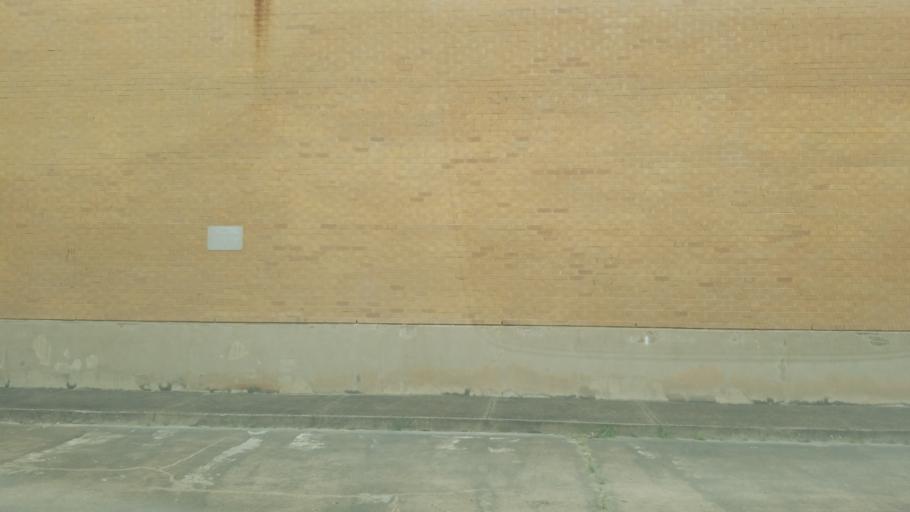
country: US
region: Texas
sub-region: Dallas County
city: Farmers Branch
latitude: 32.8753
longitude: -96.8799
